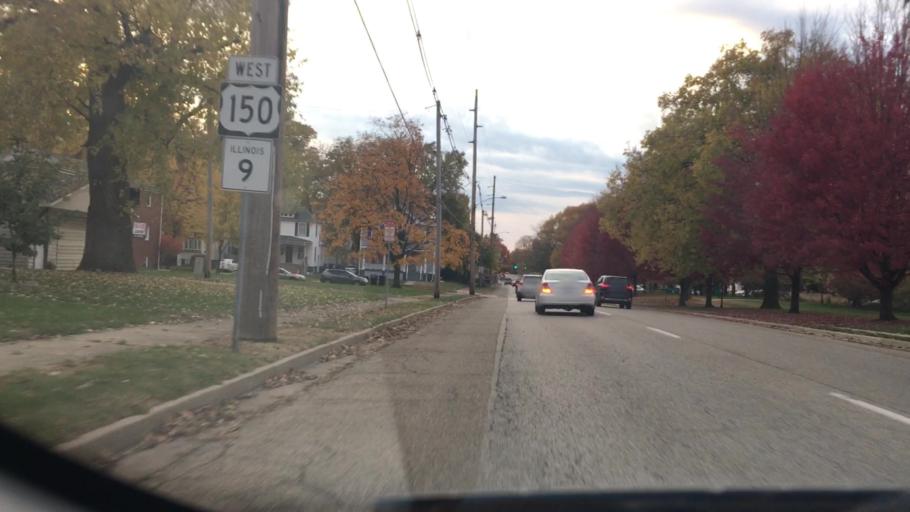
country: US
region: Illinois
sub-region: McLean County
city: Bloomington
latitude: 40.4881
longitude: -88.9901
